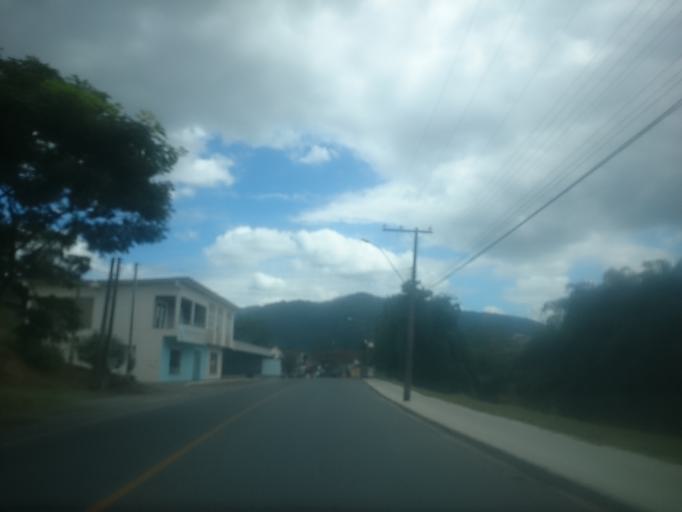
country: BR
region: Santa Catarina
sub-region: Pomerode
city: Pomerode
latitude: -26.7229
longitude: -49.1689
